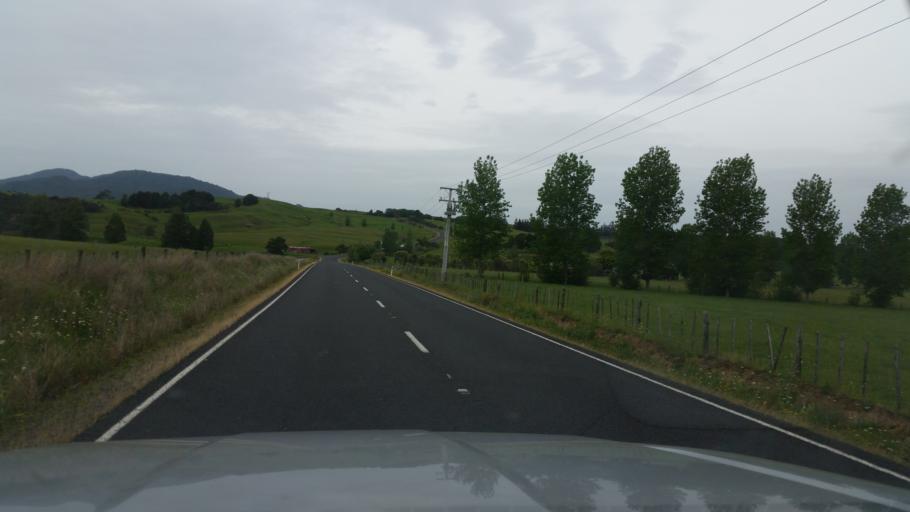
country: NZ
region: Northland
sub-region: Far North District
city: Kaitaia
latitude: -35.2726
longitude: 173.3561
